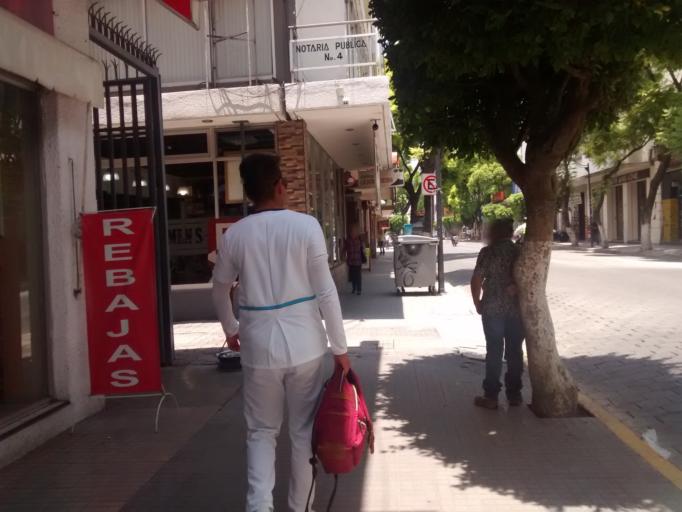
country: MX
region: Puebla
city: Tehuacan
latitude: 18.4643
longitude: -97.3940
